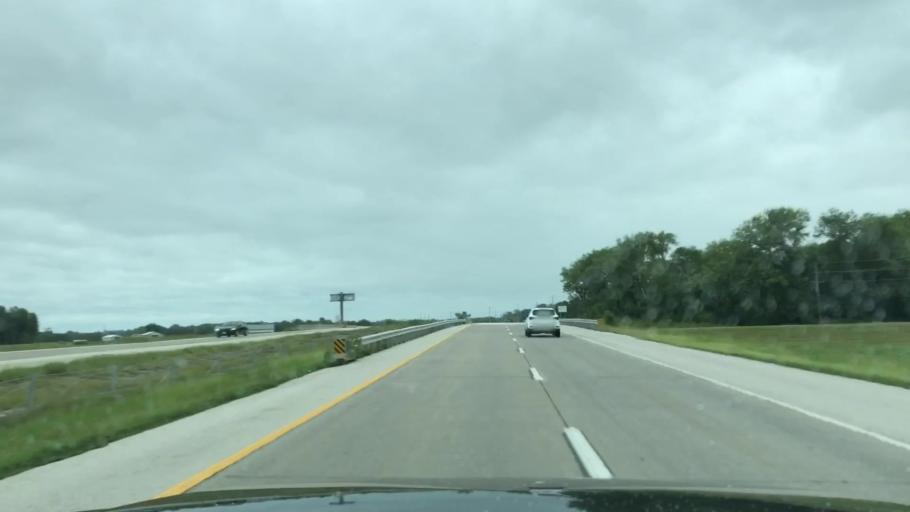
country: US
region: Missouri
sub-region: Saint Charles County
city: Saint Charles
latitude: 38.7289
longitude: -90.4938
